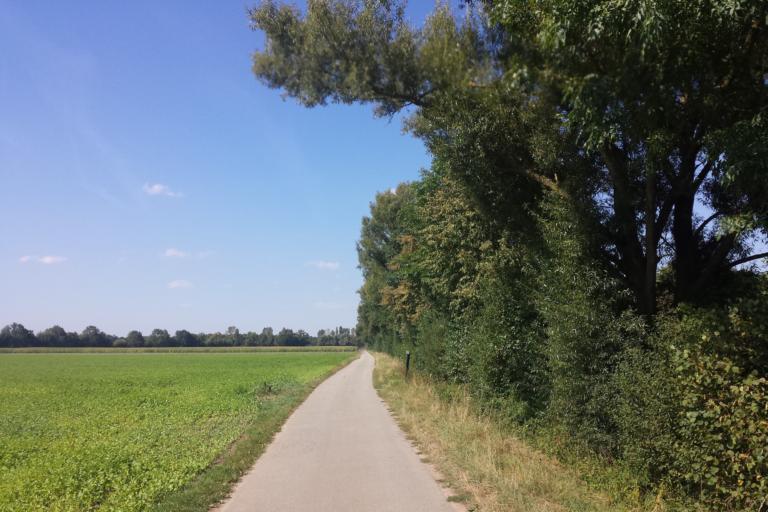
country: DE
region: Hesse
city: Lorsch
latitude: 49.6210
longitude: 8.5880
